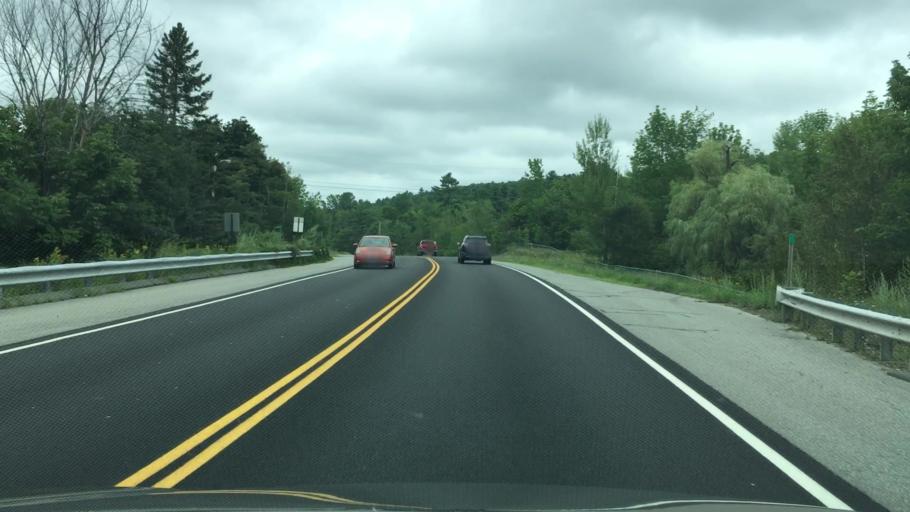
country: US
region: Maine
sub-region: Penobscot County
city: Orrington
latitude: 44.6892
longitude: -68.8107
